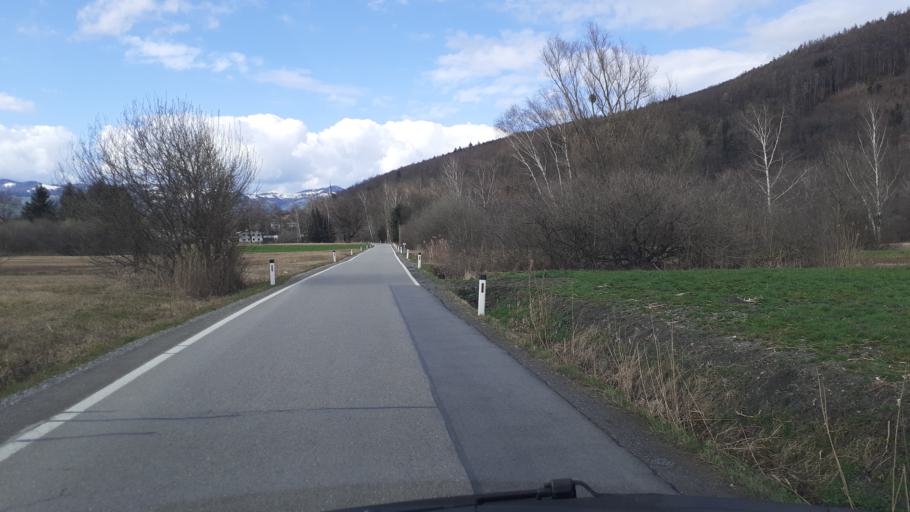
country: AT
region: Vorarlberg
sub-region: Politischer Bezirk Feldkirch
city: Koblach
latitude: 47.3262
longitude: 9.6148
